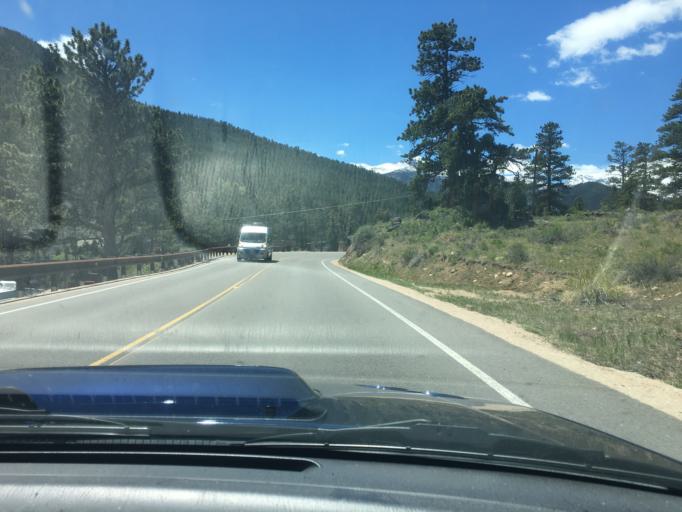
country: US
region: Colorado
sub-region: Larimer County
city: Estes Park
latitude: 40.3593
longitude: -105.5564
